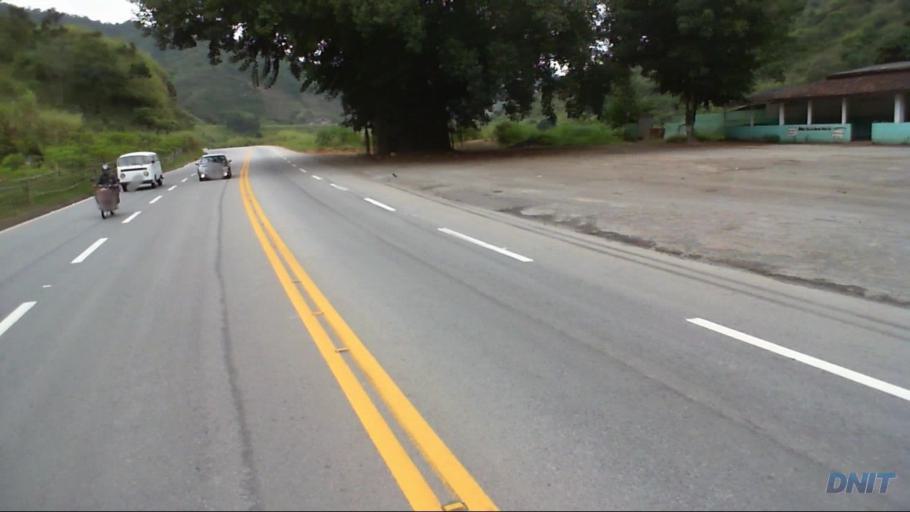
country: BR
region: Minas Gerais
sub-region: Timoteo
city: Timoteo
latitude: -19.6302
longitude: -42.8070
